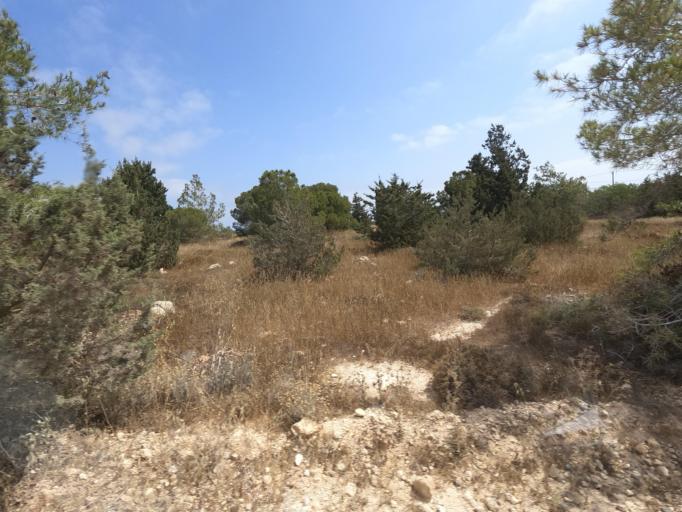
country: CY
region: Ammochostos
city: Protaras
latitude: 35.0040
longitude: 34.0379
